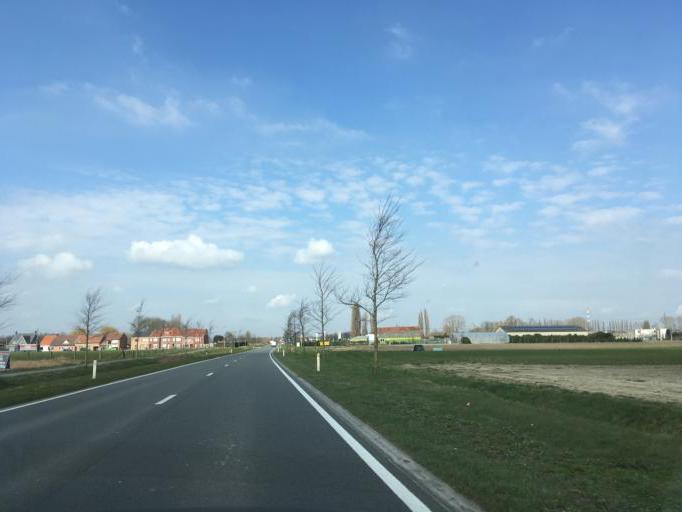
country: BE
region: Flanders
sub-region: Provincie West-Vlaanderen
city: Kuurne
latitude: 50.8723
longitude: 3.2819
